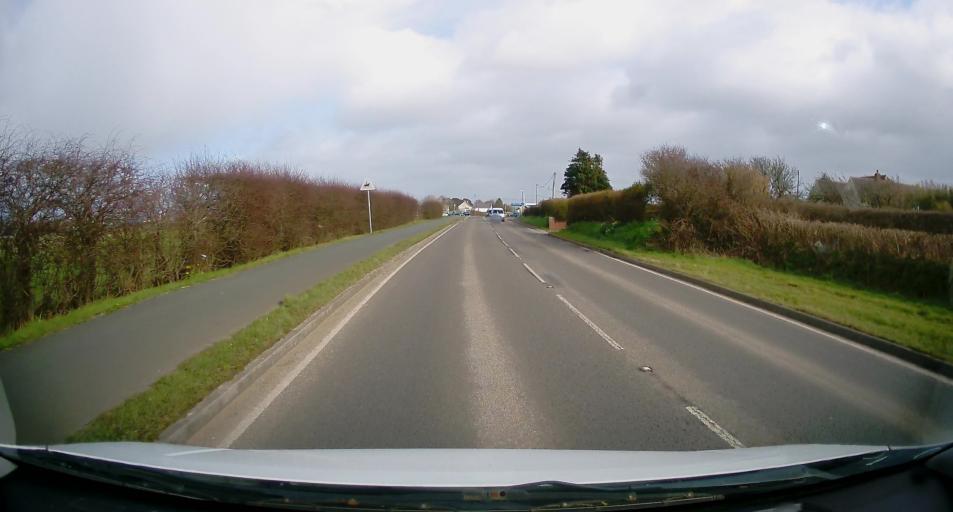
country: GB
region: Wales
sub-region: County of Ceredigion
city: Aberporth
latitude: 52.1119
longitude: -4.5672
